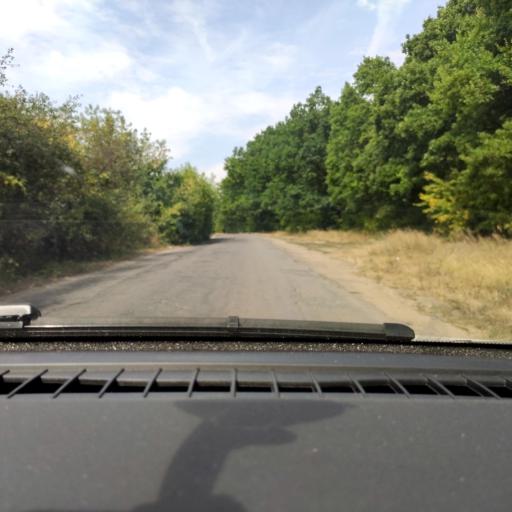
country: RU
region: Voronezj
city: Pridonskoy
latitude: 51.7367
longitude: 39.0594
